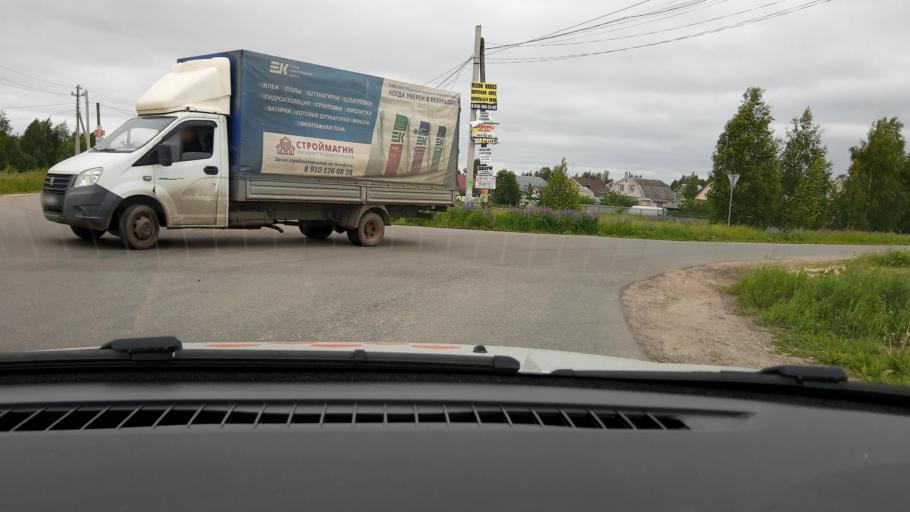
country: RU
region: Nizjnij Novgorod
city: Sitniki
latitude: 56.5245
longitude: 44.0402
